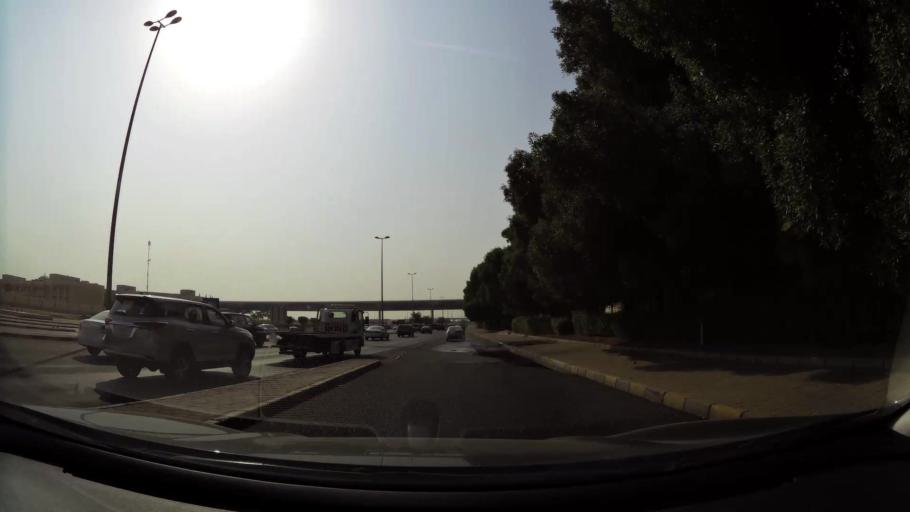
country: KW
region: Al Asimah
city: Ar Rabiyah
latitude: 29.2779
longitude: 47.9069
